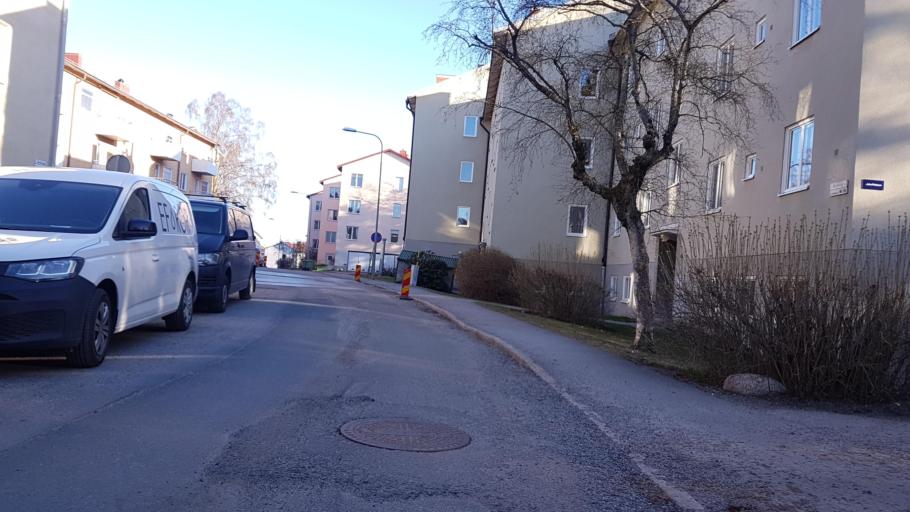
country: SE
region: Stockholm
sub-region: Stockholms Kommun
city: Arsta
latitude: 59.2645
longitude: 18.0770
